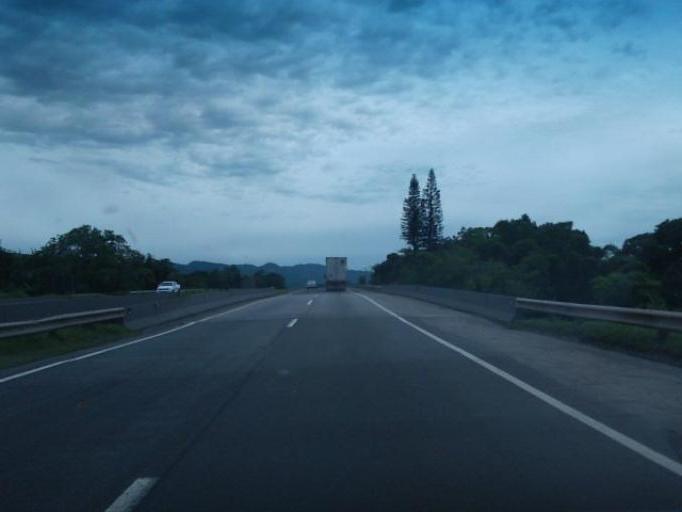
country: BR
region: Sao Paulo
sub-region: Miracatu
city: Miracatu
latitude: -24.2449
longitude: -47.3671
